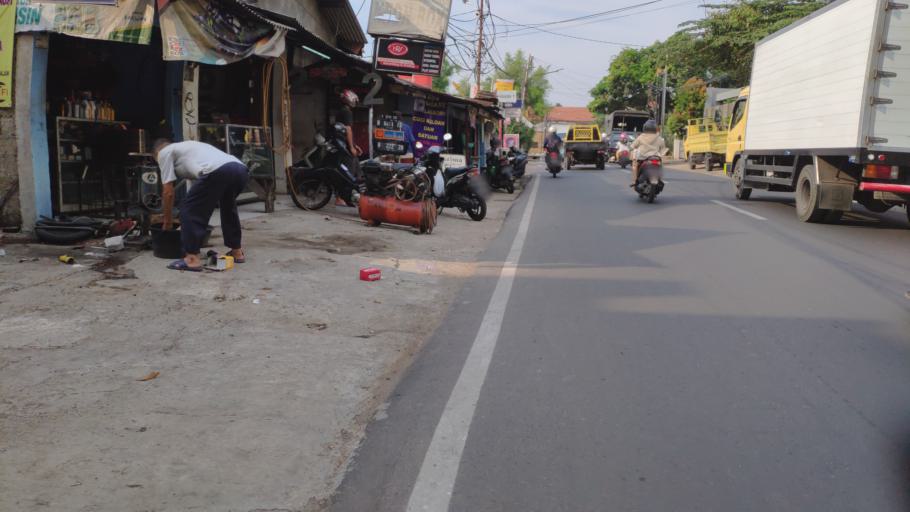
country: ID
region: West Java
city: Pamulang
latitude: -6.3139
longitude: 106.8126
